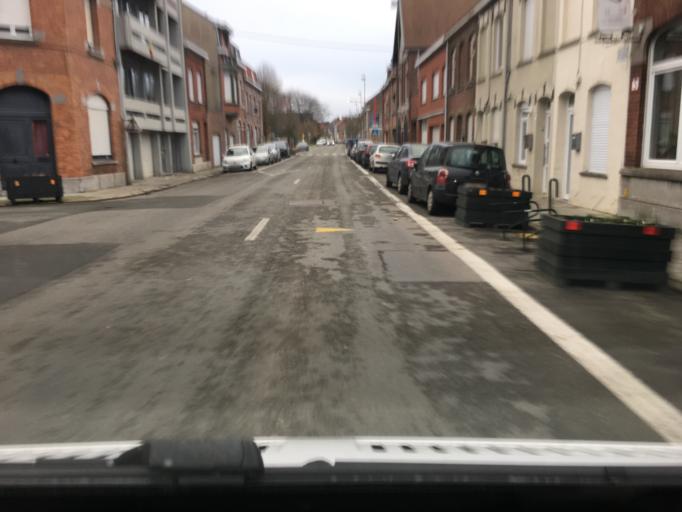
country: FR
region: Nord-Pas-de-Calais
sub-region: Departement du Nord
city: Comines
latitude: 50.7708
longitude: 3.0055
